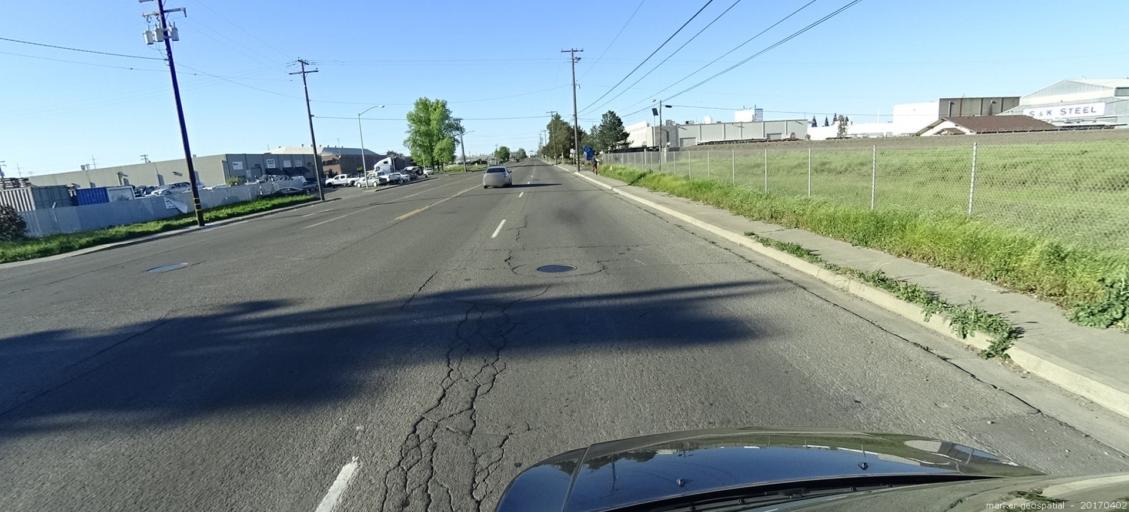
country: US
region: California
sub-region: Sacramento County
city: Rosemont
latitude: 38.5276
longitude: -121.3907
